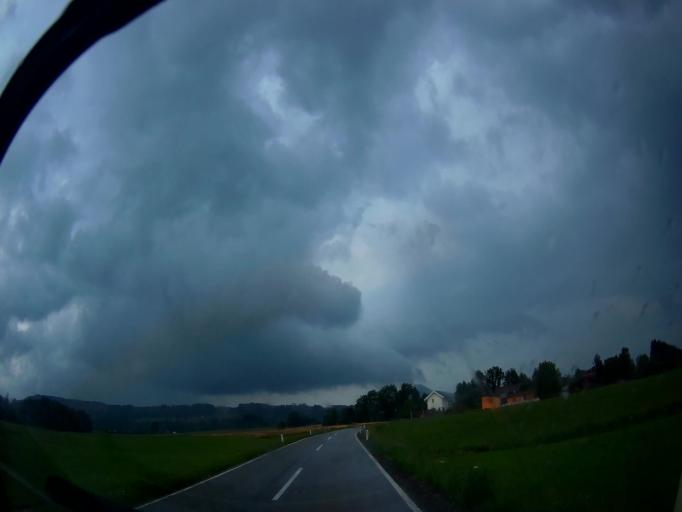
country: AT
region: Salzburg
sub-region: Politischer Bezirk Salzburg-Umgebung
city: Mattsee
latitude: 48.0000
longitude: 13.1220
